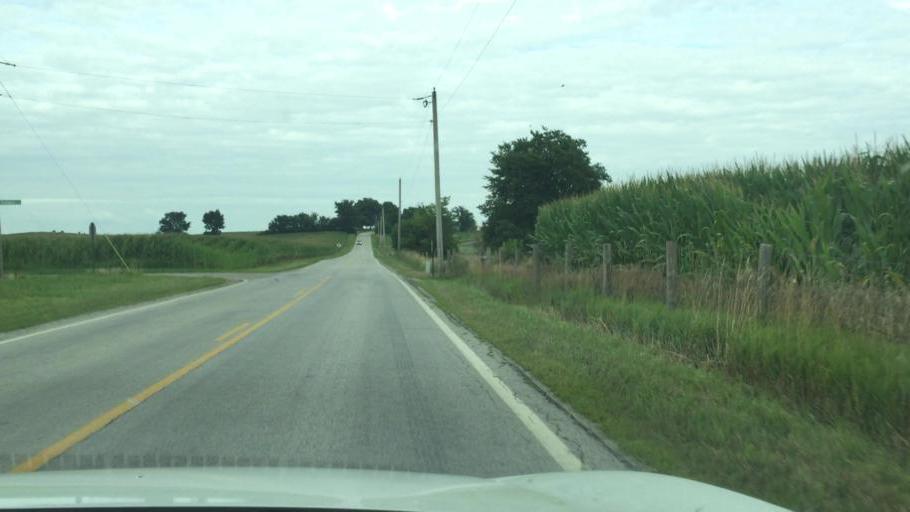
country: US
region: Ohio
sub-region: Clark County
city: Northridge
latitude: 39.9909
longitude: -83.6954
